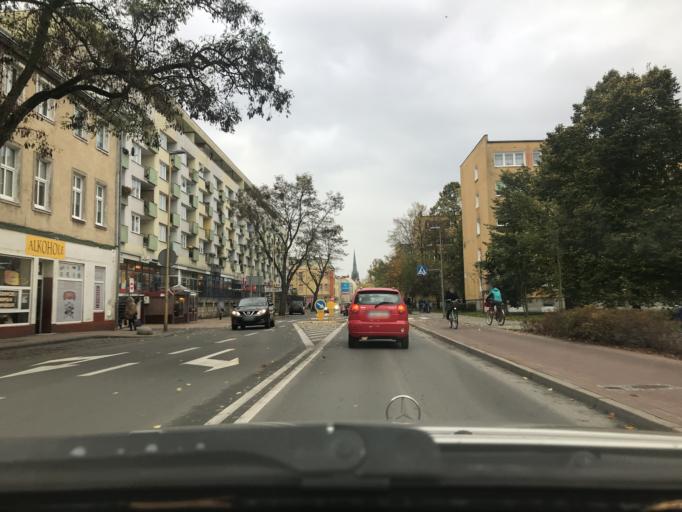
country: PL
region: West Pomeranian Voivodeship
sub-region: Swinoujscie
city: Swinoujscie
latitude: 53.9119
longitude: 14.2413
